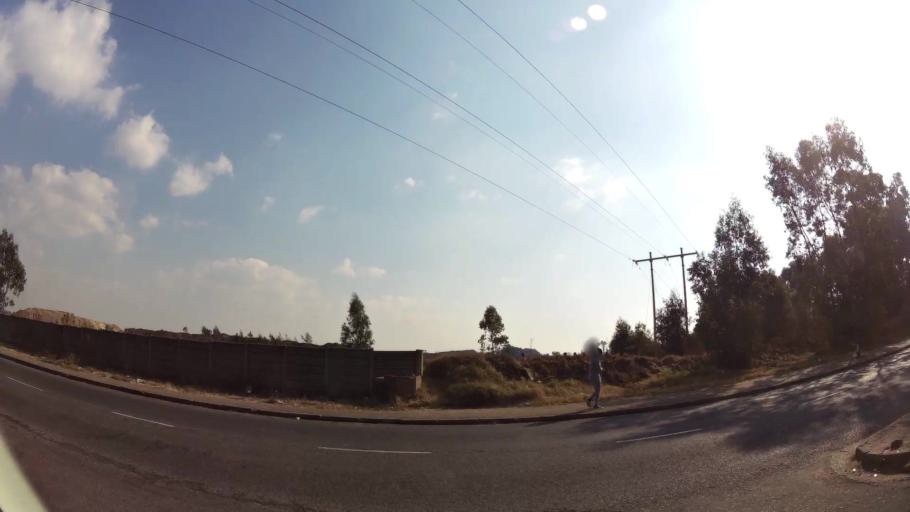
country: ZA
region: Gauteng
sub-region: Ekurhuleni Metropolitan Municipality
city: Boksburg
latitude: -26.2115
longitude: 28.2536
